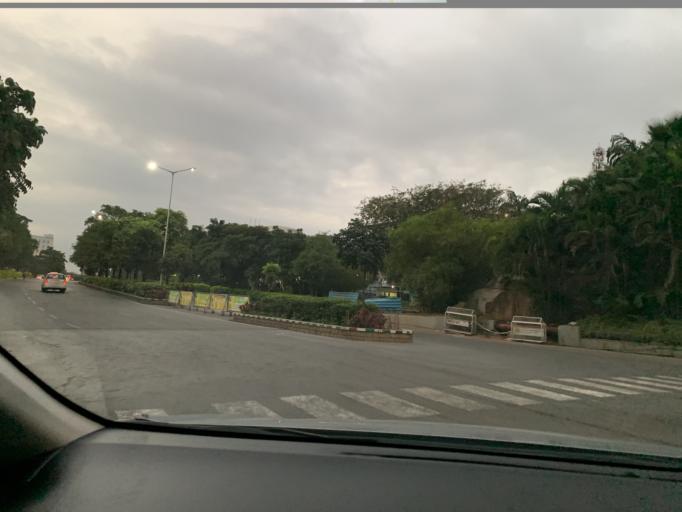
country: IN
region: Telangana
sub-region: Rangareddi
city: Kukatpalli
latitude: 17.4403
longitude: 78.3794
